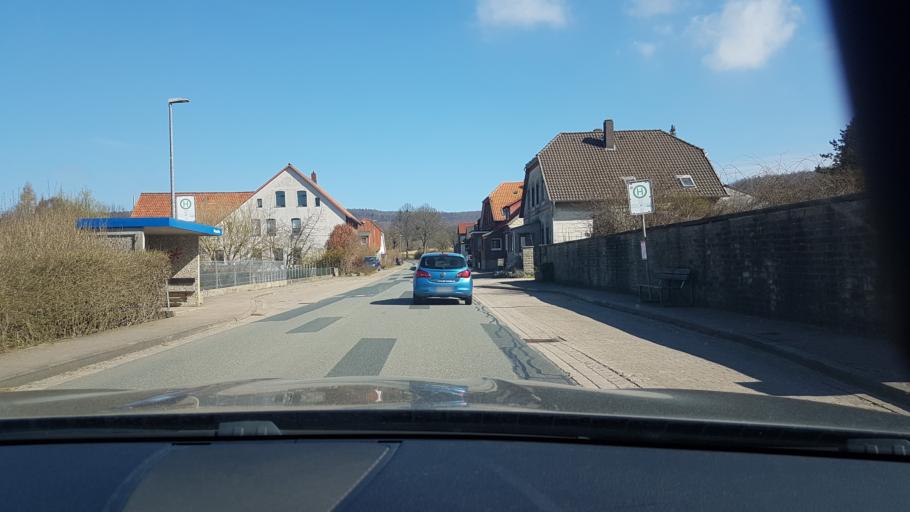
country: DE
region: Lower Saxony
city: Coppenbrugge
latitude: 52.1353
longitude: 9.5668
